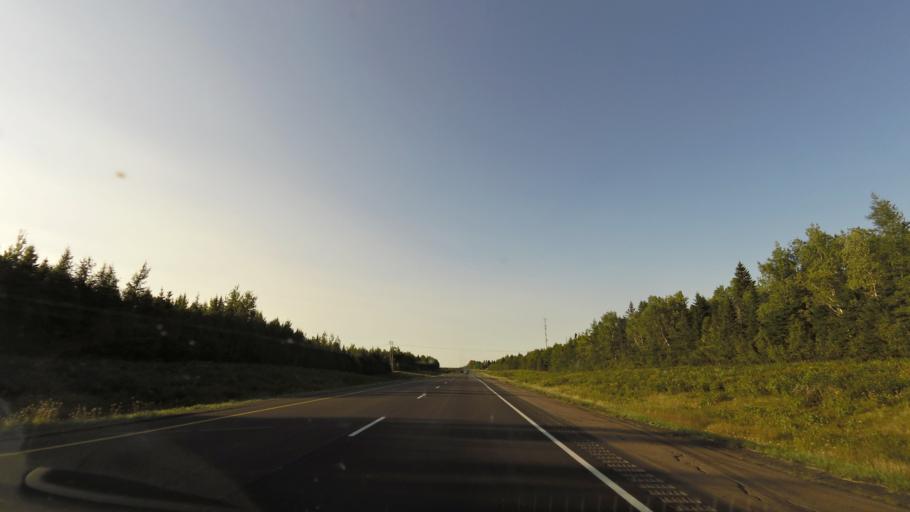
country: CA
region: New Brunswick
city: Dieppe
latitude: 46.0784
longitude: -64.5928
